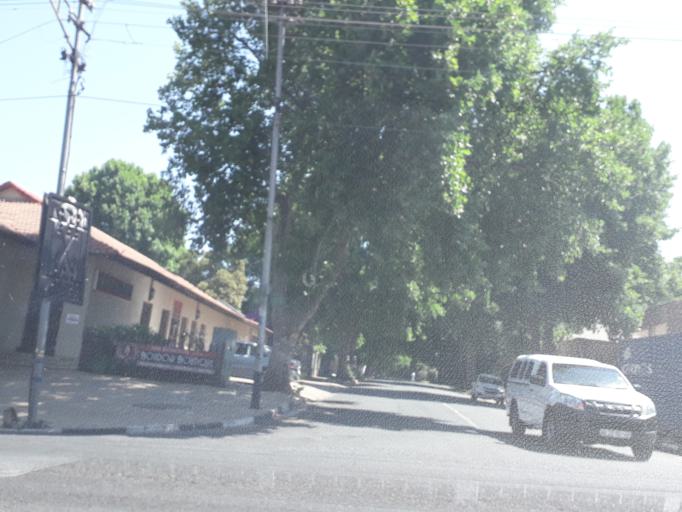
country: ZA
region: Gauteng
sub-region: City of Johannesburg Metropolitan Municipality
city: Johannesburg
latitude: -26.1439
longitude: 28.0207
